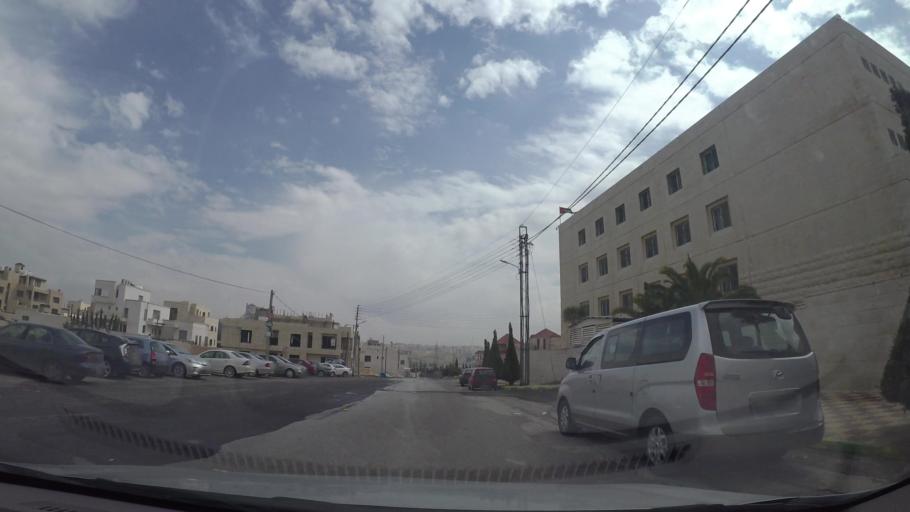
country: JO
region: Amman
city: Umm as Summaq
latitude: 31.9117
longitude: 35.8536
